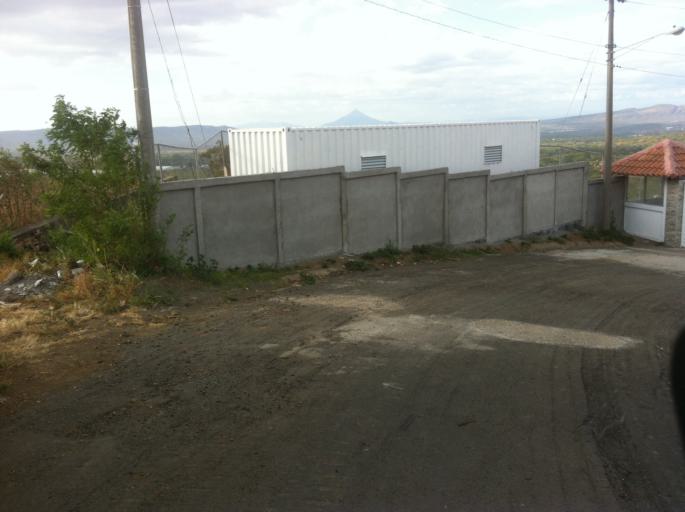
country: NI
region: Managua
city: Ciudad Sandino
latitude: 12.1019
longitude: -86.3287
